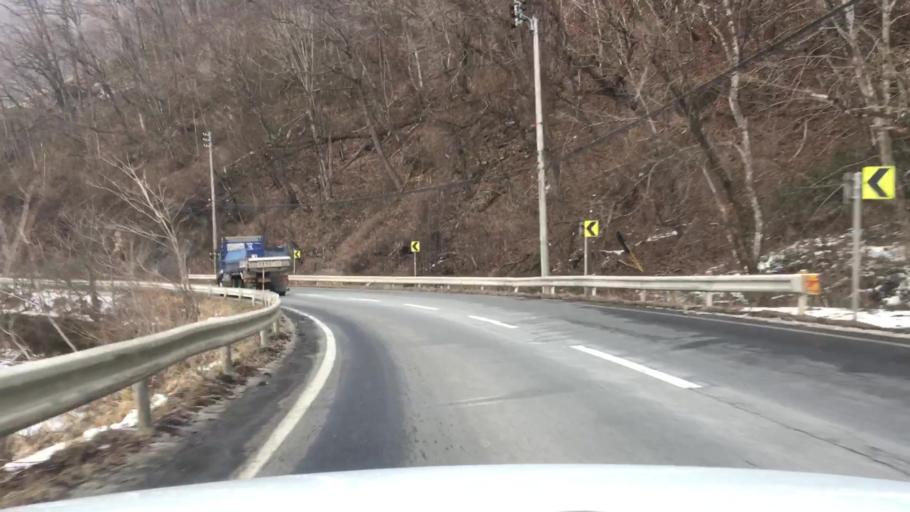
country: JP
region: Iwate
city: Tono
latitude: 39.6213
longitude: 141.4760
